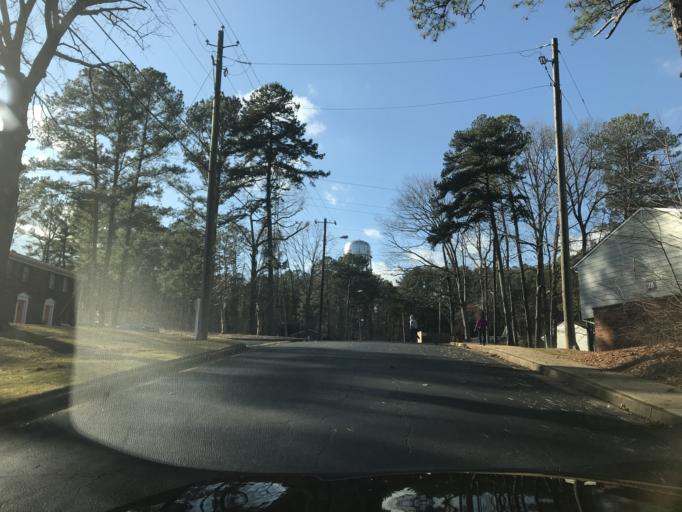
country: US
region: Georgia
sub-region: Fulton County
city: College Park
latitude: 33.6471
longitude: -84.4763
